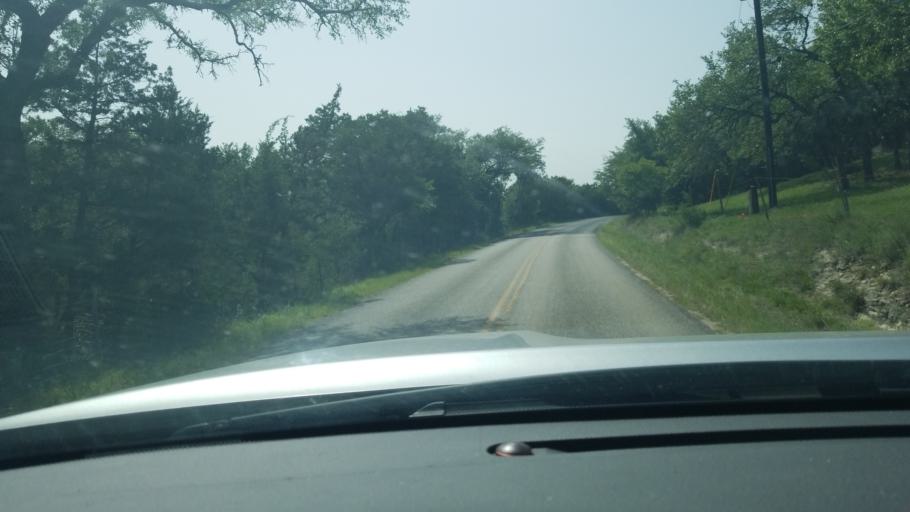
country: US
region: Texas
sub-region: Comal County
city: Bulverde
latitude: 29.7939
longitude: -98.4405
